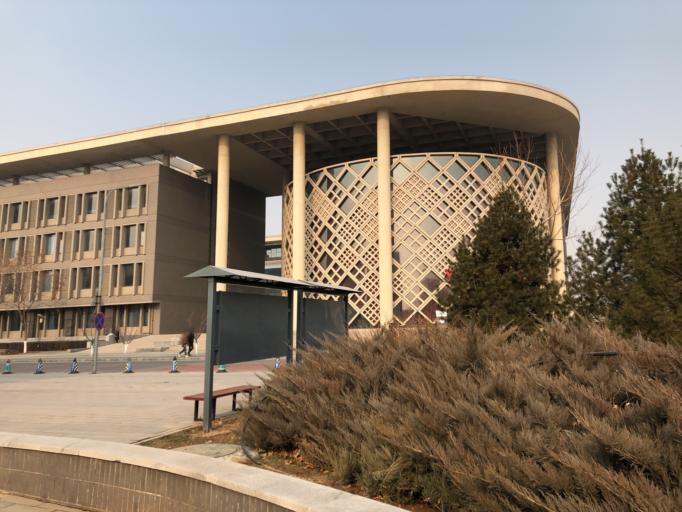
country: CN
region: Beijing
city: Daxing
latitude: 39.7467
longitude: 116.2799
